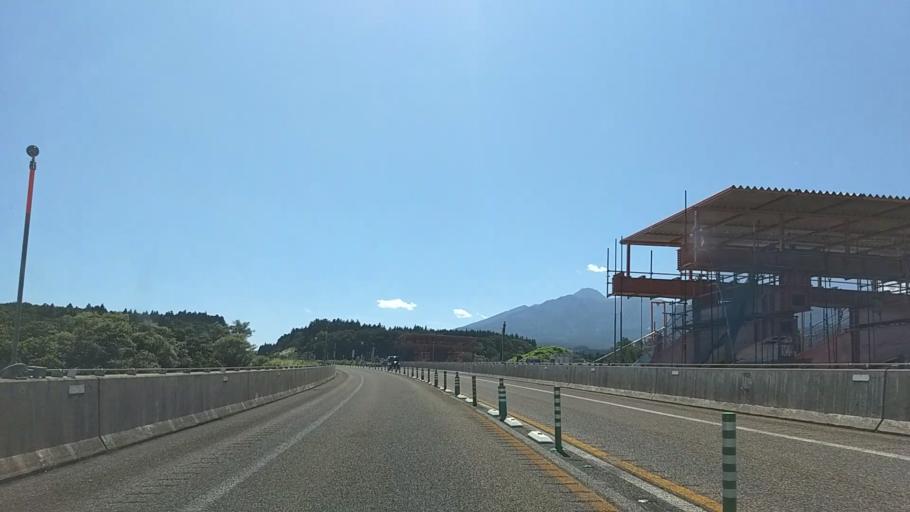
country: JP
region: Niigata
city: Arai
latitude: 37.0062
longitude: 138.2087
